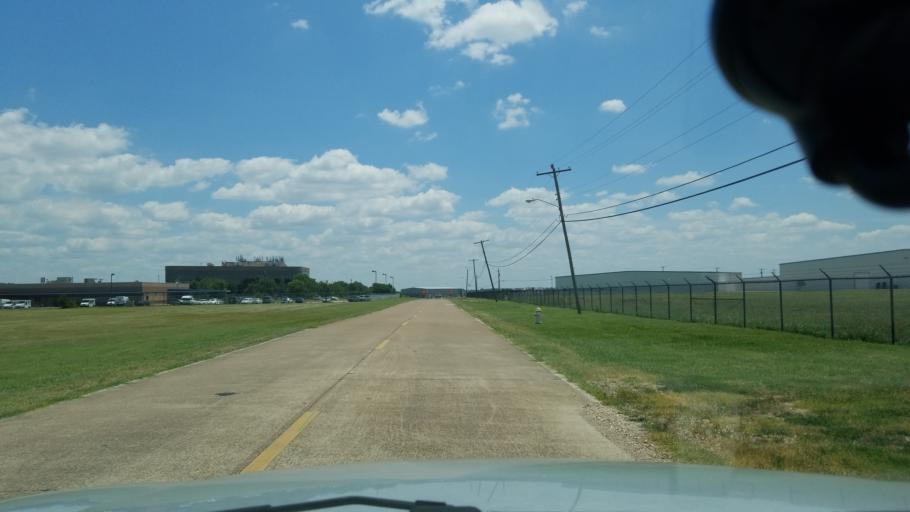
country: US
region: Texas
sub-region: Dallas County
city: Duncanville
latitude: 32.6815
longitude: -96.8590
